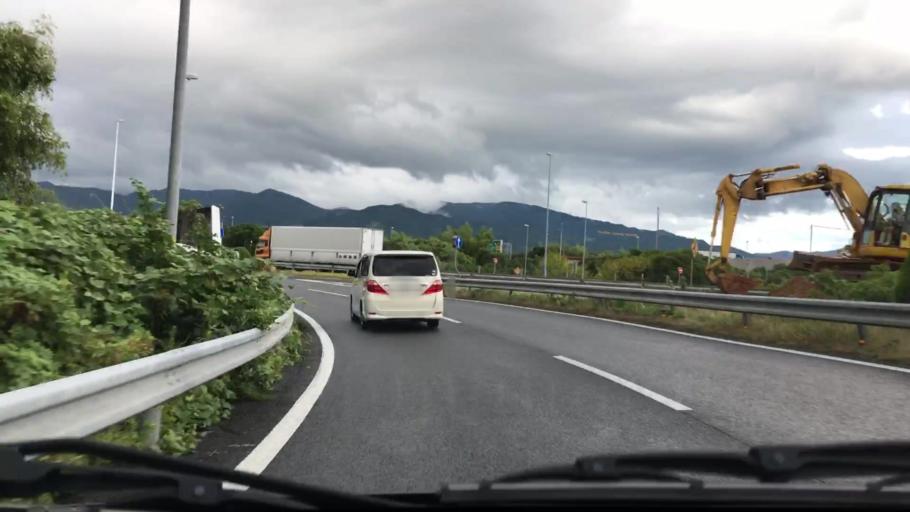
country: JP
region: Fukuoka
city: Sasaguri
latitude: 33.6298
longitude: 130.4891
